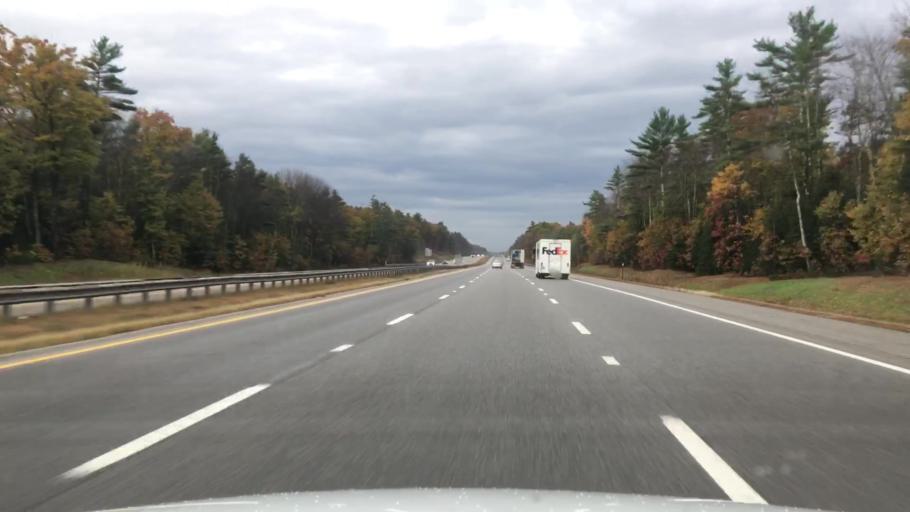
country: US
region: Maine
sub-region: York County
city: West Kennebunk
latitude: 43.4604
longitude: -70.5252
